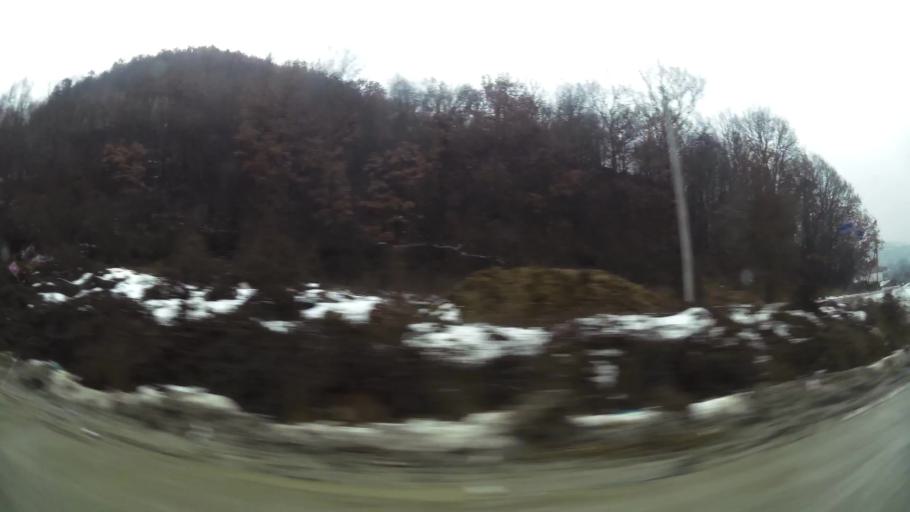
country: XK
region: Ferizaj
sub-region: Hani i Elezit
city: Hani i Elezit
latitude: 42.1627
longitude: 21.2777
